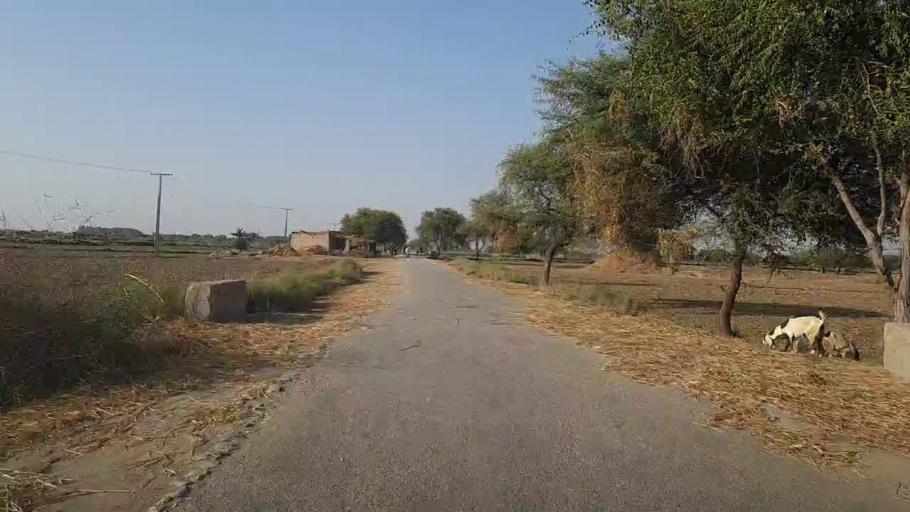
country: PK
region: Sindh
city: Kashmor
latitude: 28.4150
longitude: 69.4109
